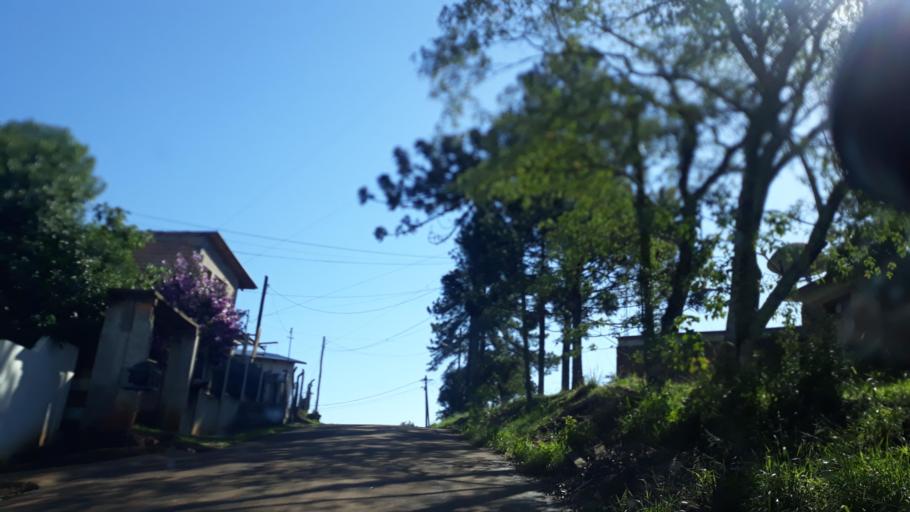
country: AR
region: Misiones
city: Bernardo de Irigoyen
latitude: -26.2593
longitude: -53.6458
